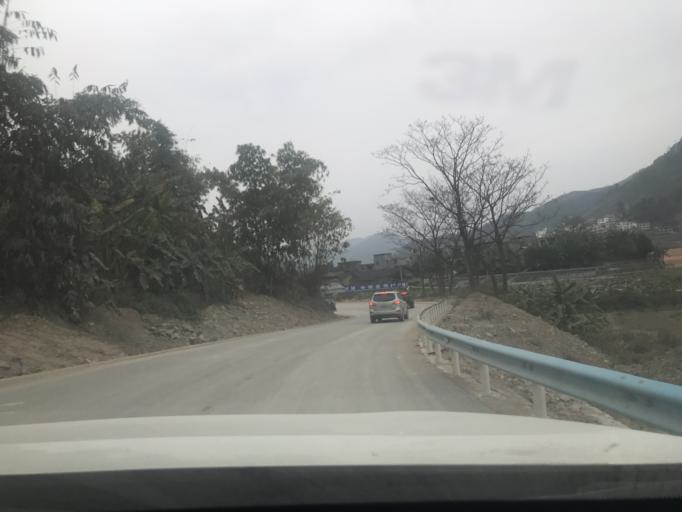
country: CN
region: Guangxi Zhuangzu Zizhiqu
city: Xinzhou
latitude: 25.0134
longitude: 105.8599
